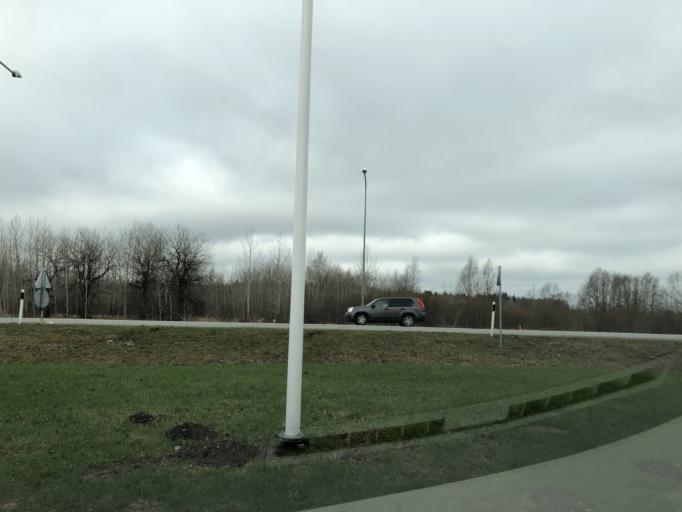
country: EE
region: Laeaene-Virumaa
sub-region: Rakvere linn
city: Rakvere
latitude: 59.3659
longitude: 26.3379
